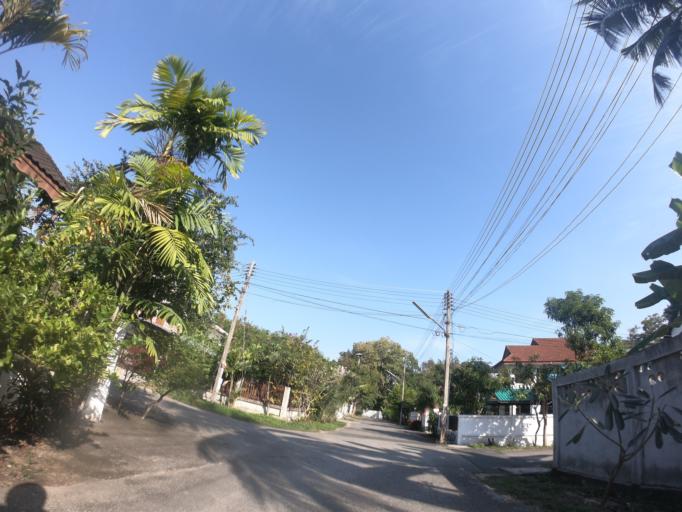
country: TH
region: Chiang Mai
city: Chiang Mai
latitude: 18.7791
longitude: 99.0338
